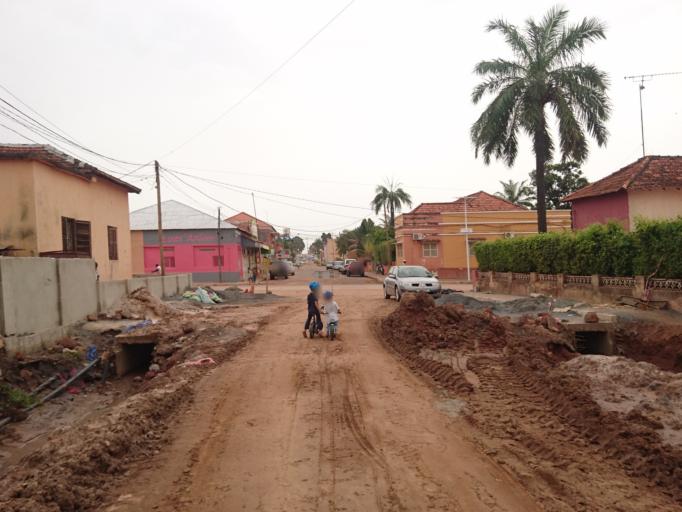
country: GW
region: Bissau
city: Bissau
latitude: 11.8592
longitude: -15.5847
